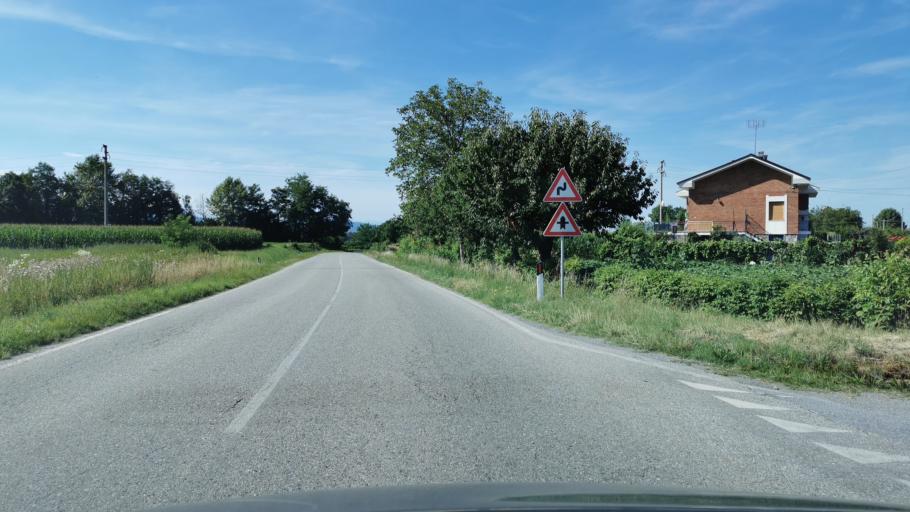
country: IT
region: Piedmont
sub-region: Provincia di Cuneo
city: Cuneo
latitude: 44.3639
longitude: 7.5607
